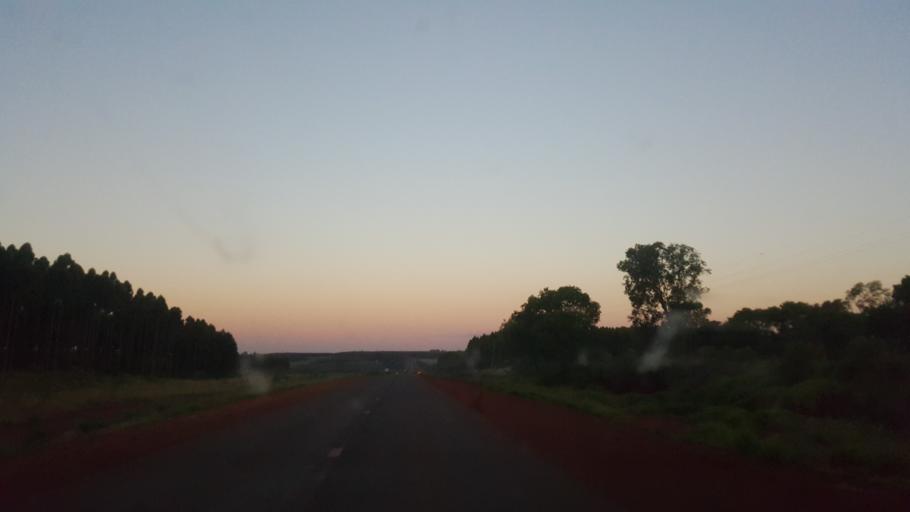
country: AR
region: Corrientes
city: Garruchos
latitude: -28.2415
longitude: -55.8305
